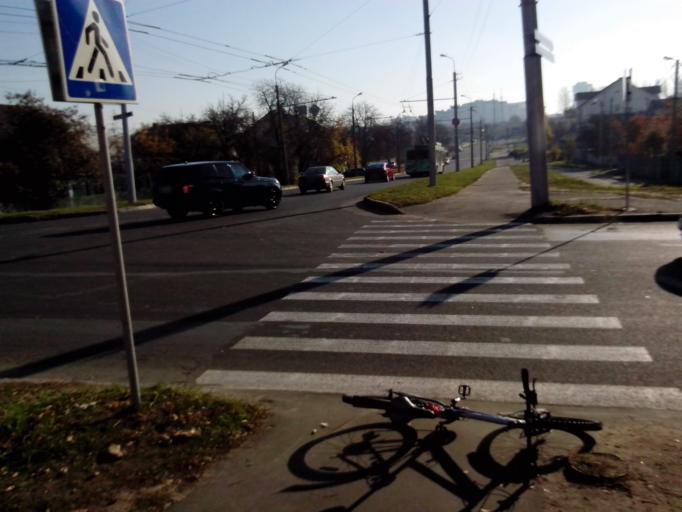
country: BY
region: Minsk
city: Bal'shavik
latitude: 53.9522
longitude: 27.5966
